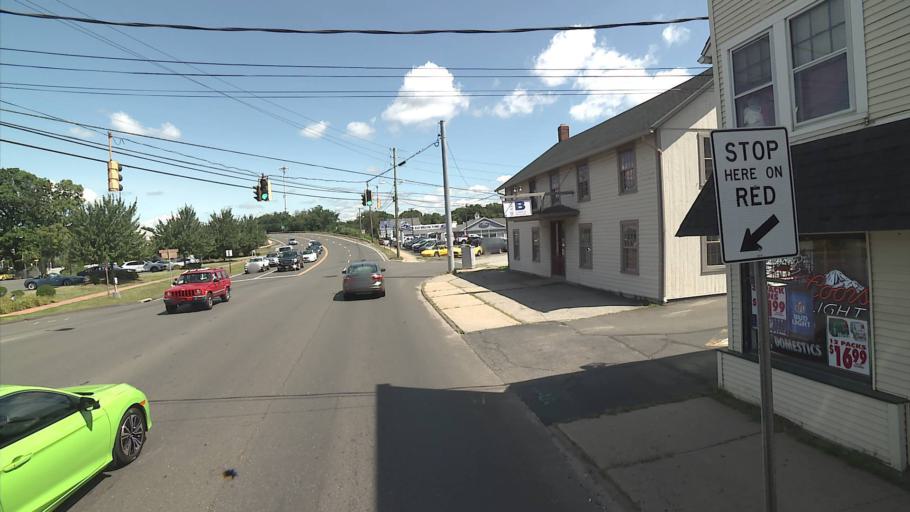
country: US
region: Connecticut
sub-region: Middlesex County
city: Old Saybrook
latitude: 41.2990
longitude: -72.3758
